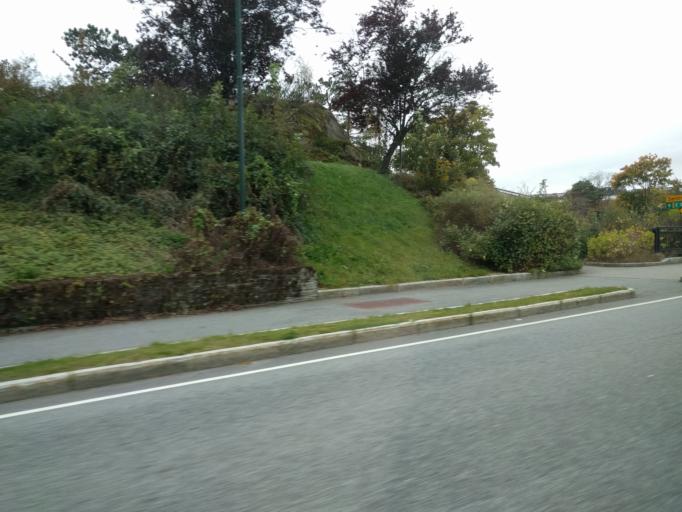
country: NO
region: Vest-Agder
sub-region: Kristiansand
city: Kristiansand
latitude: 58.1487
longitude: 7.9724
